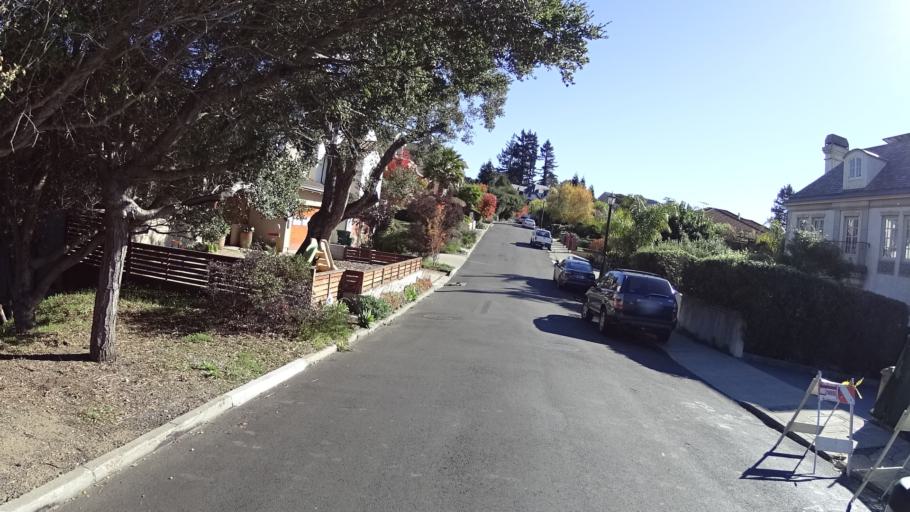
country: US
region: California
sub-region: Alameda County
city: Piedmont
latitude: 37.8465
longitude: -122.2333
